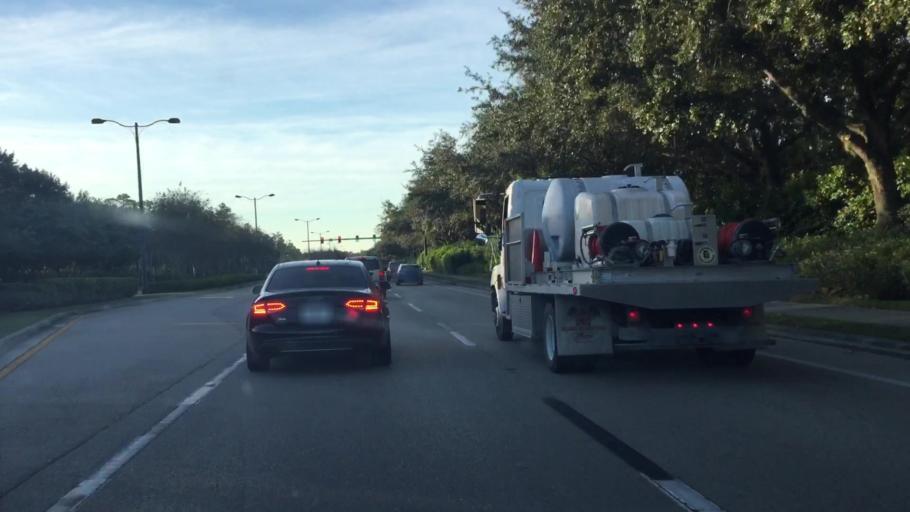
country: US
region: Florida
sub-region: Lee County
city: Three Oaks
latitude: 26.4716
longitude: -81.7864
